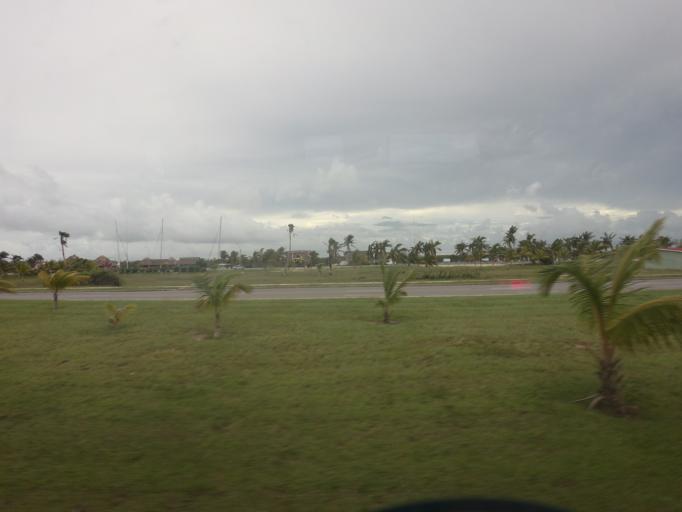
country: CU
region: Matanzas
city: Varadero
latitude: 23.1823
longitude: -81.1822
